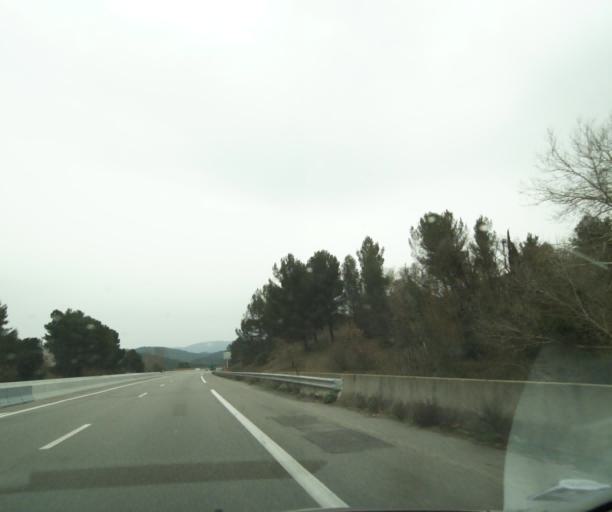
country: FR
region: Provence-Alpes-Cote d'Azur
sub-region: Departement des Bouches-du-Rhone
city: La Bouilladisse
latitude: 43.3917
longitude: 5.5906
